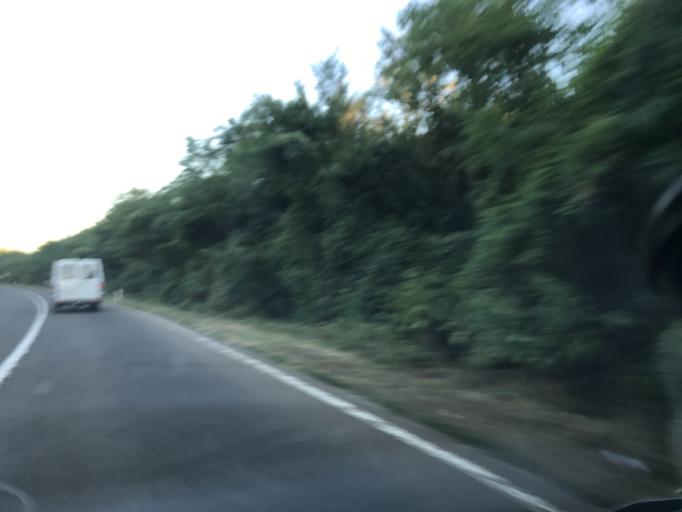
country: RS
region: Central Serbia
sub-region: Branicevski Okrug
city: Pozarevac
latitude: 44.6486
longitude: 21.2075
